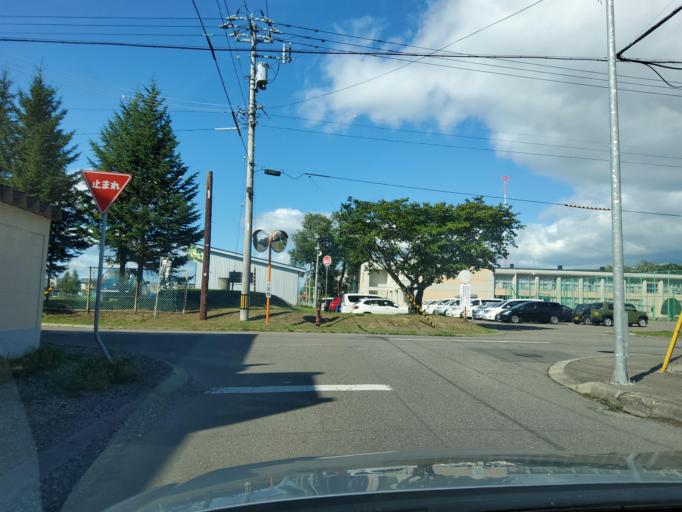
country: JP
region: Hokkaido
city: Obihiro
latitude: 42.9529
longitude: 143.1949
